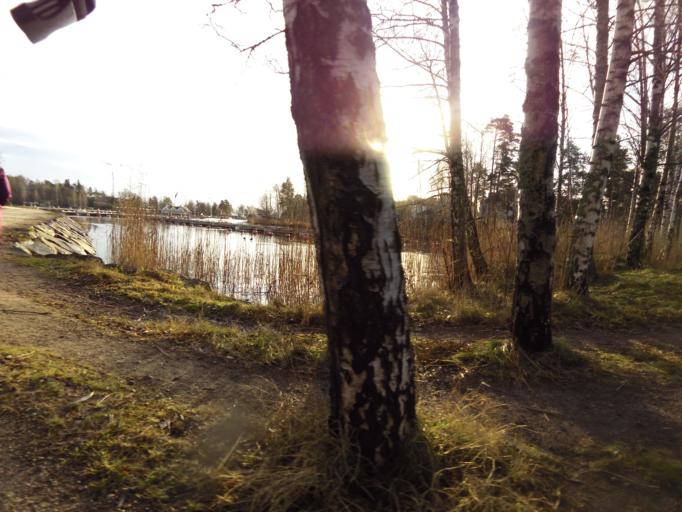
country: FI
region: Uusimaa
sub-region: Helsinki
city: Koukkuniemi
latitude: 60.1576
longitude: 24.7668
